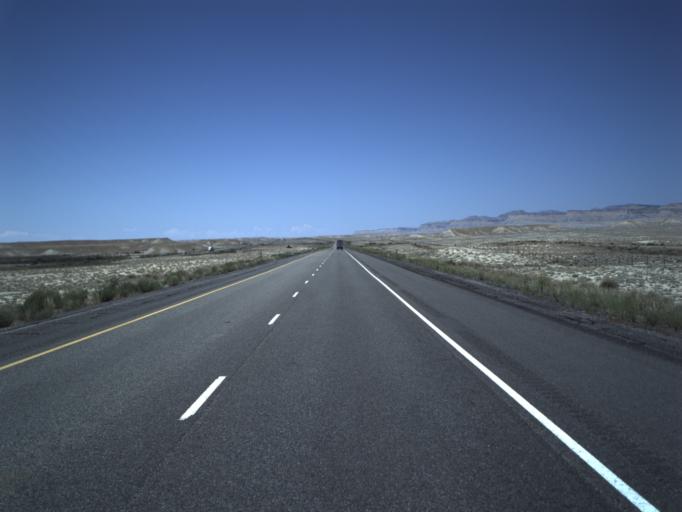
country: US
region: Utah
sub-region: Grand County
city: Moab
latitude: 38.9394
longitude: -109.4961
